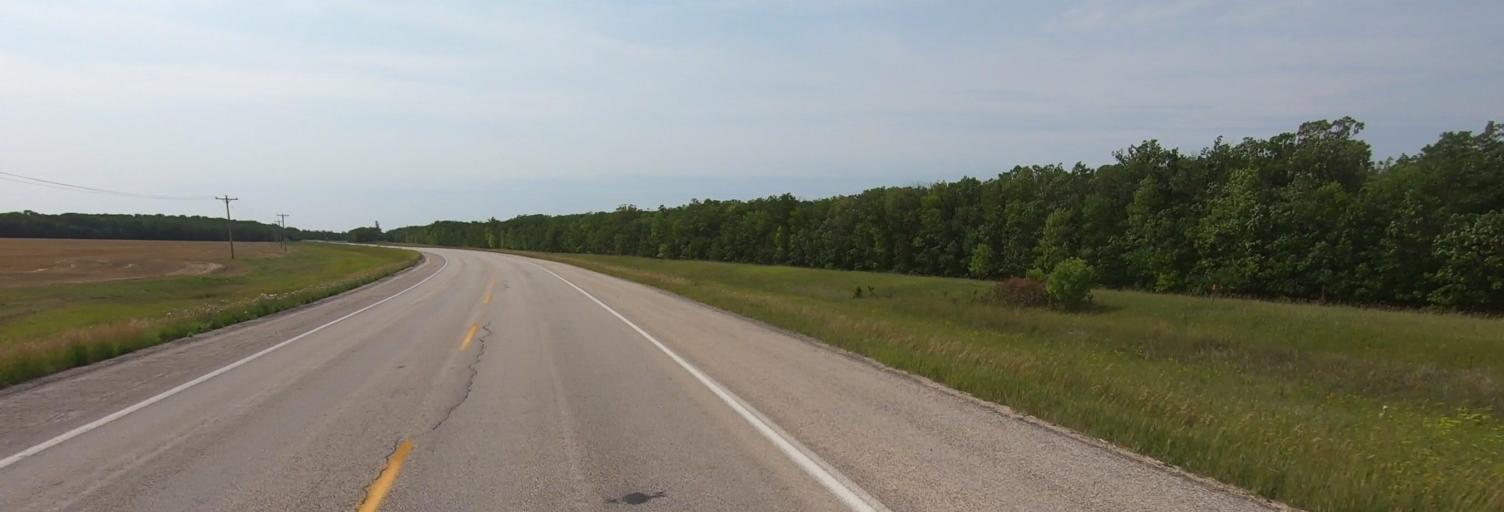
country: CA
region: Manitoba
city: Niverville
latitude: 49.5975
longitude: -97.1347
